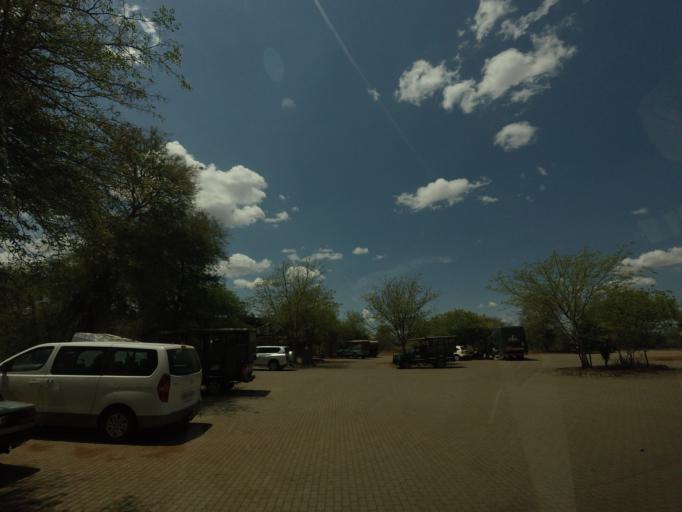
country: ZA
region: Limpopo
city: Thulamahashi
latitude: -24.3924
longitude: 31.7797
